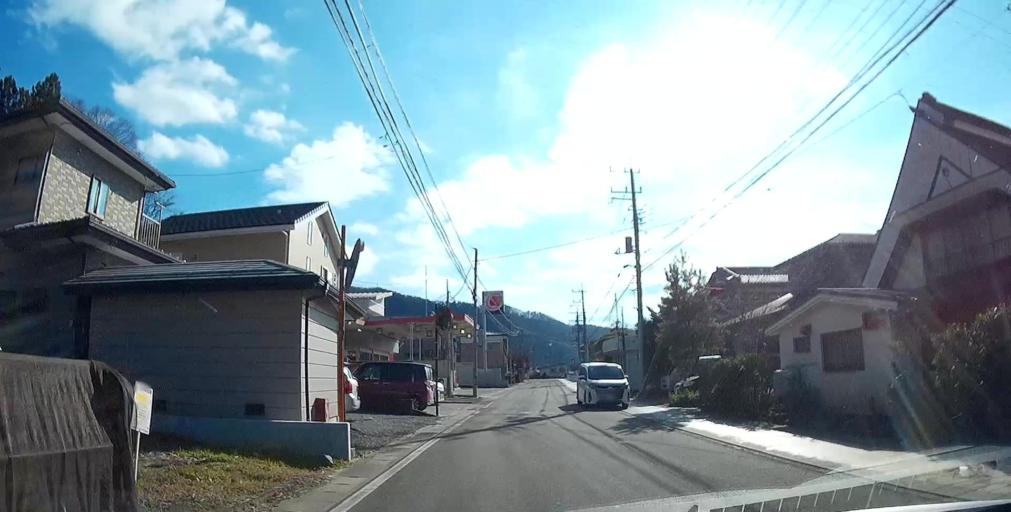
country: JP
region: Yamanashi
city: Fujikawaguchiko
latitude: 35.5275
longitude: 138.7736
